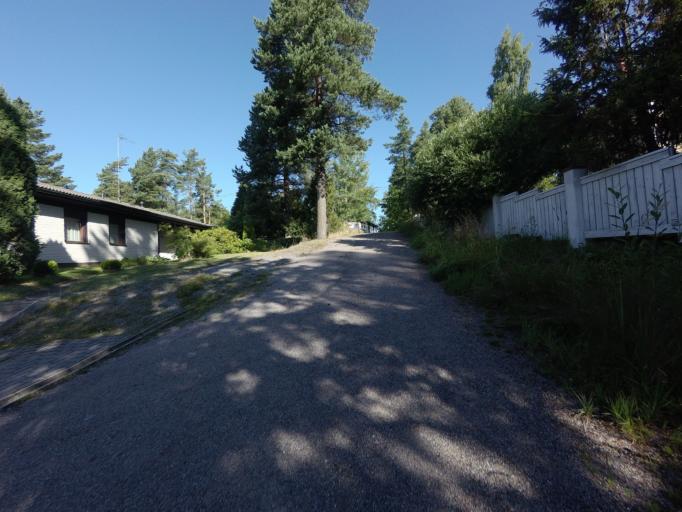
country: FI
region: Uusimaa
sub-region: Helsinki
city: Espoo
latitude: 60.1476
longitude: 24.6788
